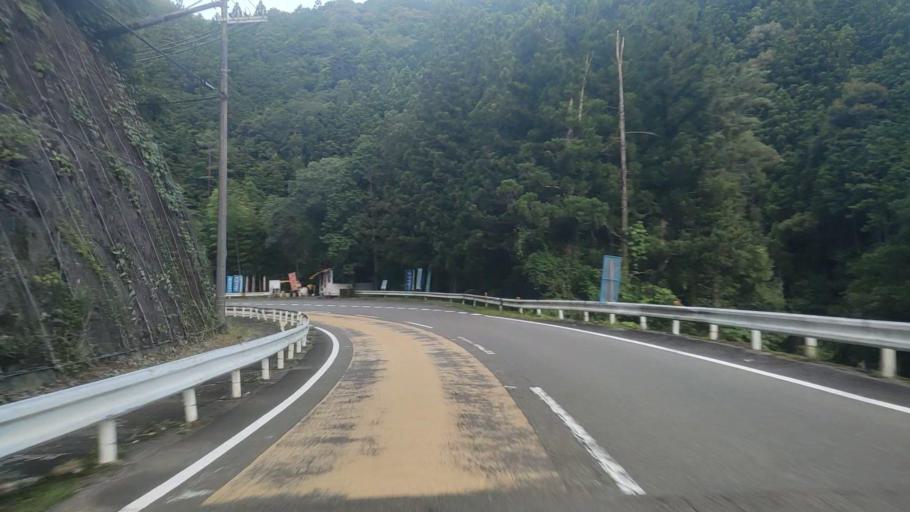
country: JP
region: Wakayama
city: Shingu
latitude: 33.8057
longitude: 135.7332
